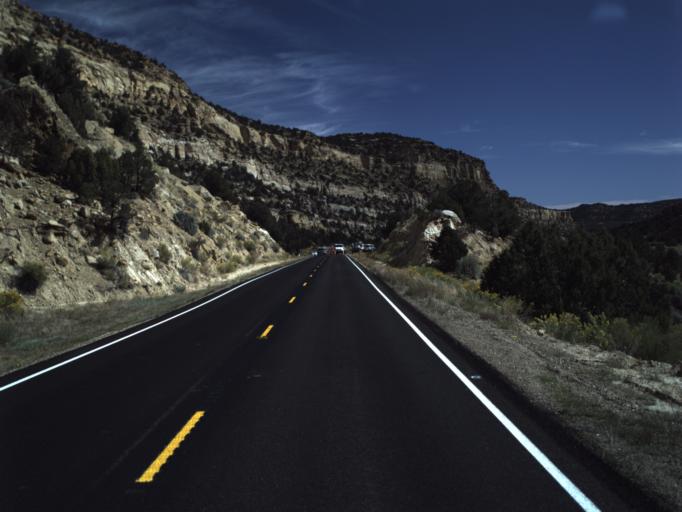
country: US
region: Utah
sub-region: Wayne County
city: Loa
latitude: 37.7335
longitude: -111.7535
